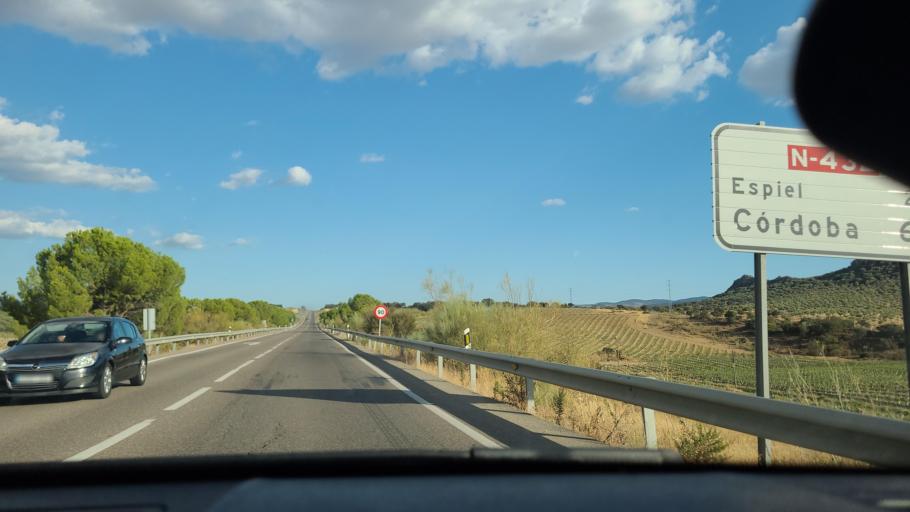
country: ES
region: Andalusia
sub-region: Province of Cordoba
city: Belmez
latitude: 38.2613
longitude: -5.1791
